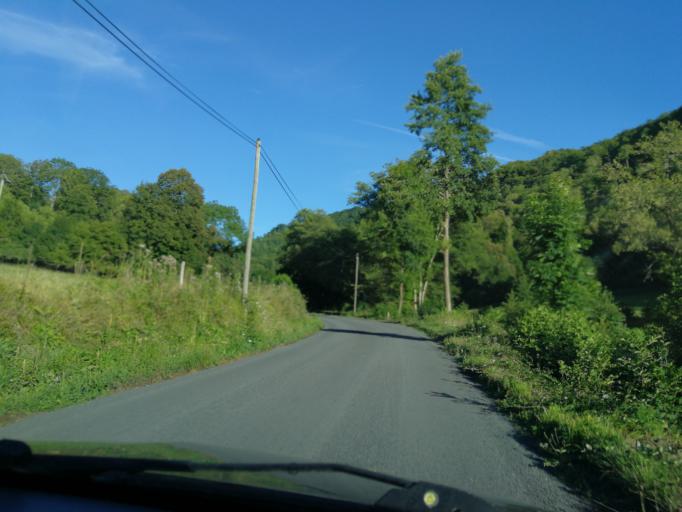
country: FR
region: Auvergne
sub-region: Departement du Cantal
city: Saint-Cernin
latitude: 45.1016
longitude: 2.5335
